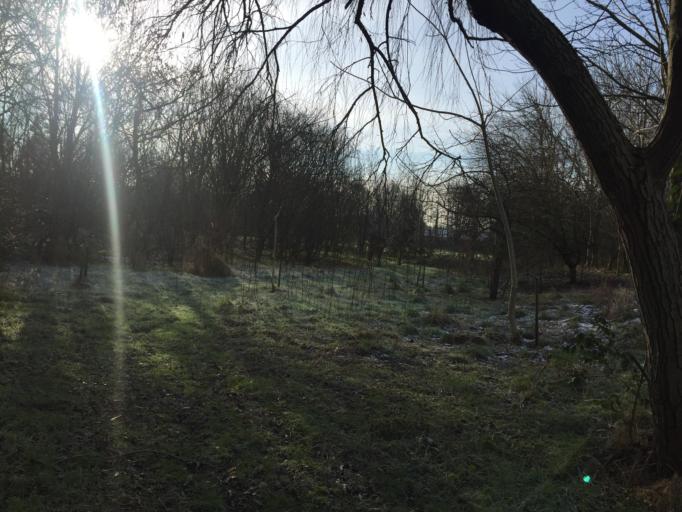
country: NL
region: North Holland
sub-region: Gemeente Beemster
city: Halfweg
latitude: 52.5206
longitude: 4.9280
